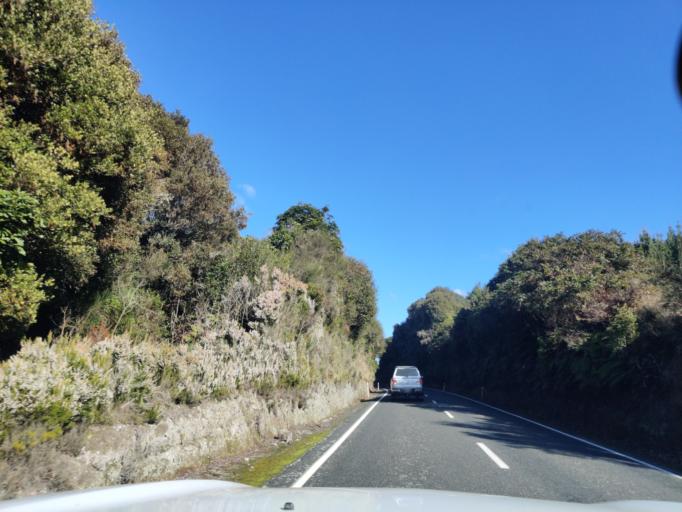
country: NZ
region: Waikato
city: Turangi
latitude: -38.7170
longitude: 175.6582
